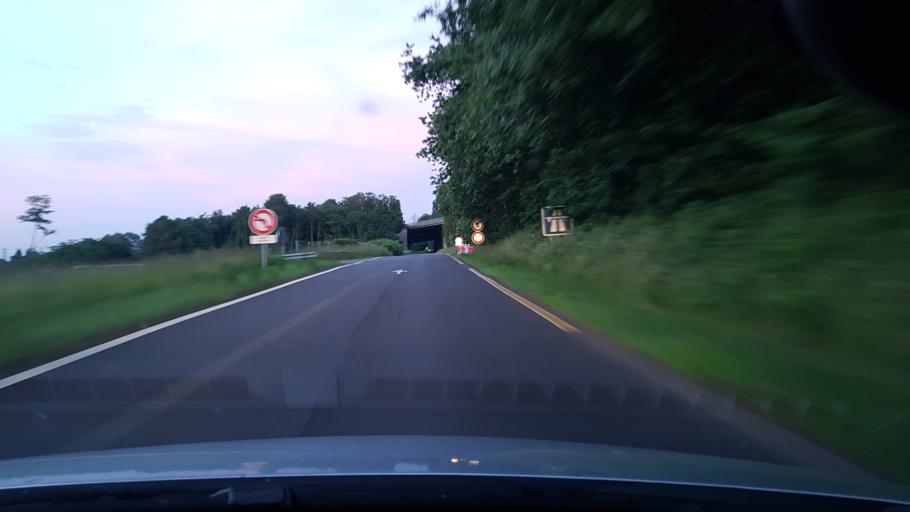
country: FR
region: Ile-de-France
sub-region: Departement de l'Essonne
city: Villebon-sur-Yvette
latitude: 48.6971
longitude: 2.2351
